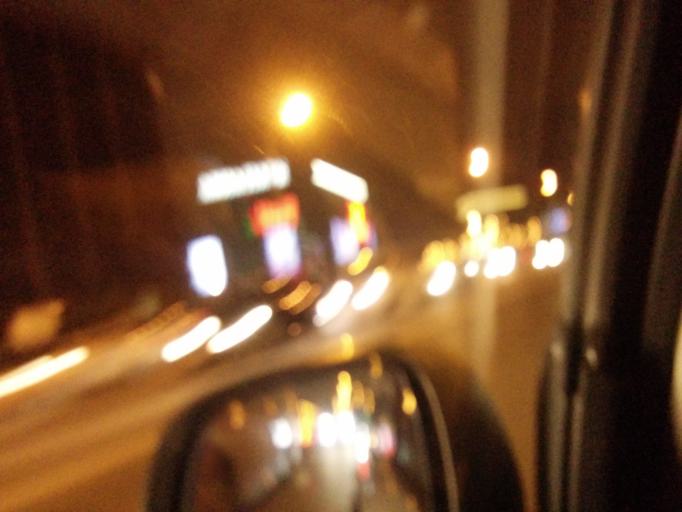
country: RU
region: Moscow
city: Sokol
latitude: 55.7899
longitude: 37.5388
